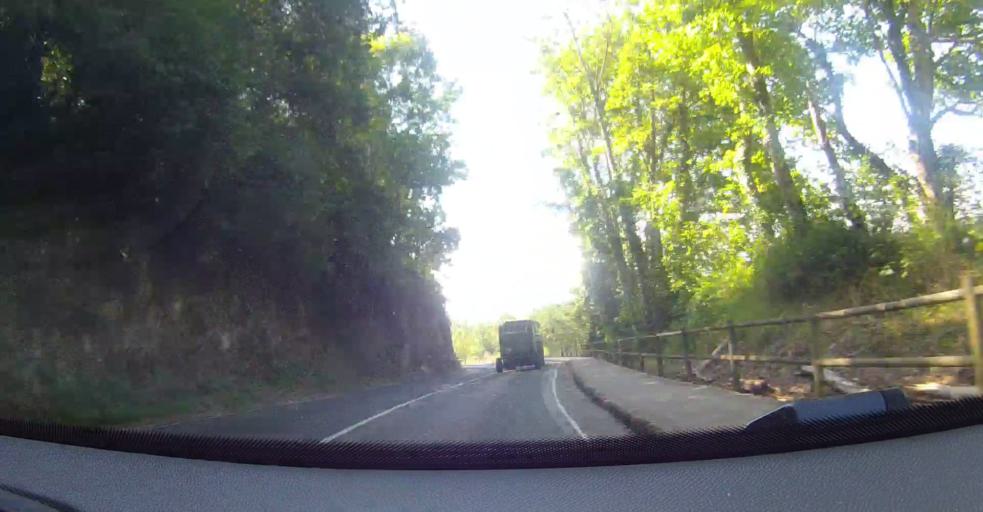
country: ES
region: Asturias
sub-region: Province of Asturias
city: Colunga
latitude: 43.4876
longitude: -5.2762
